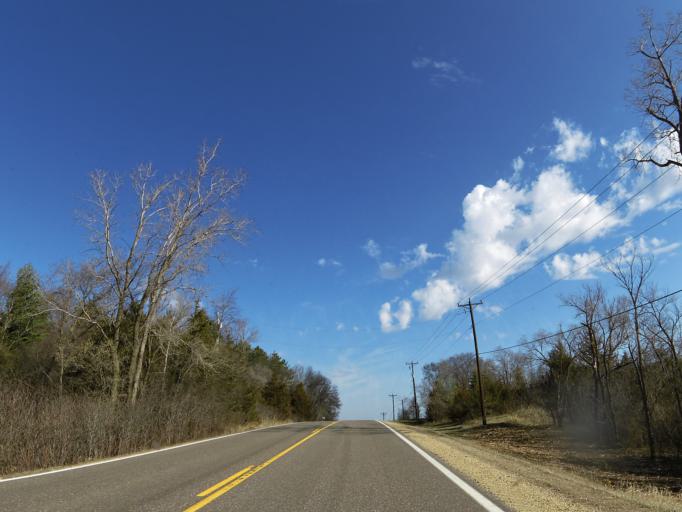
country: US
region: Minnesota
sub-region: Washington County
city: Afton
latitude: 44.9214
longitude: -92.8428
